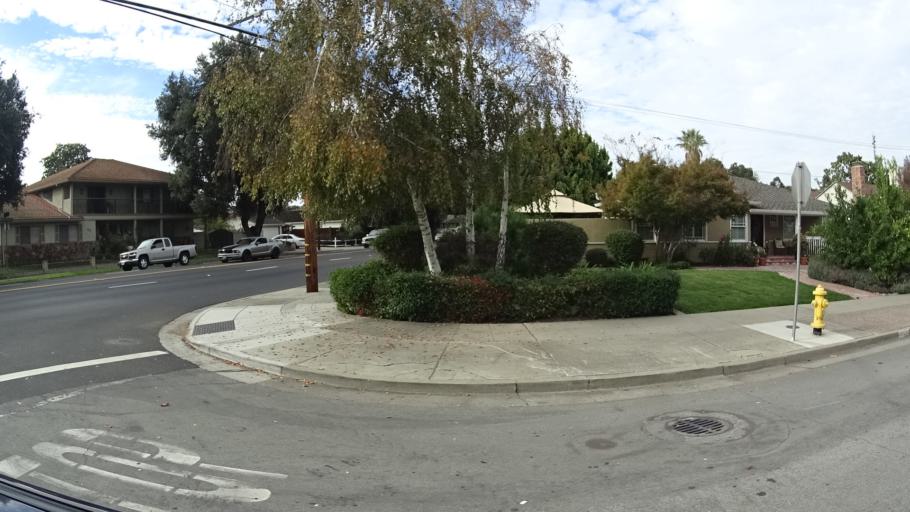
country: US
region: California
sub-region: Santa Clara County
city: Burbank
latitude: 37.3296
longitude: -121.9330
